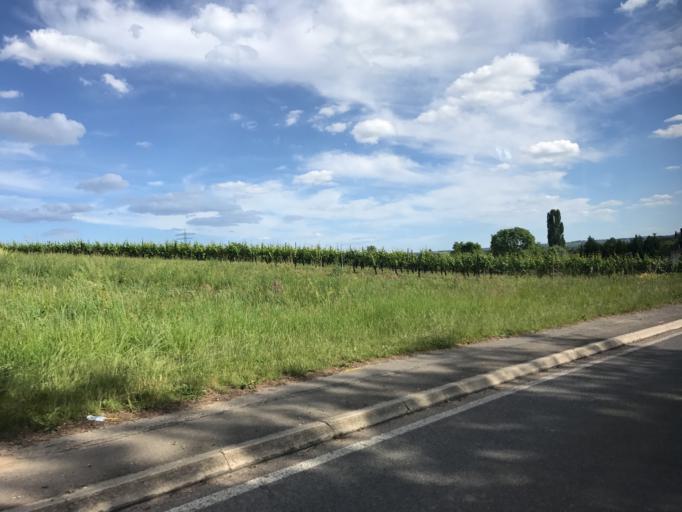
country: DE
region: Hesse
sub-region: Regierungsbezirk Darmstadt
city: Eltville
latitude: 50.0384
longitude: 8.1178
